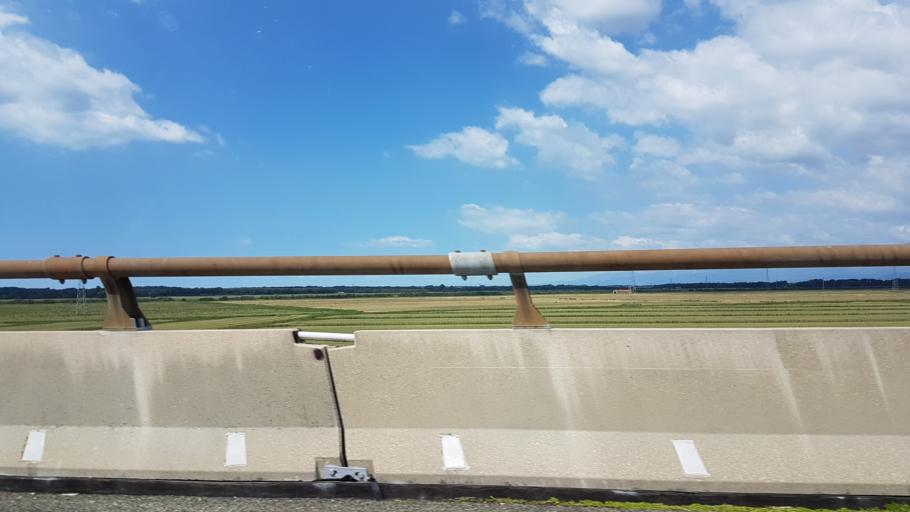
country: IT
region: Tuscany
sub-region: Provincia di Livorno
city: Guasticce
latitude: 43.6100
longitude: 10.3779
